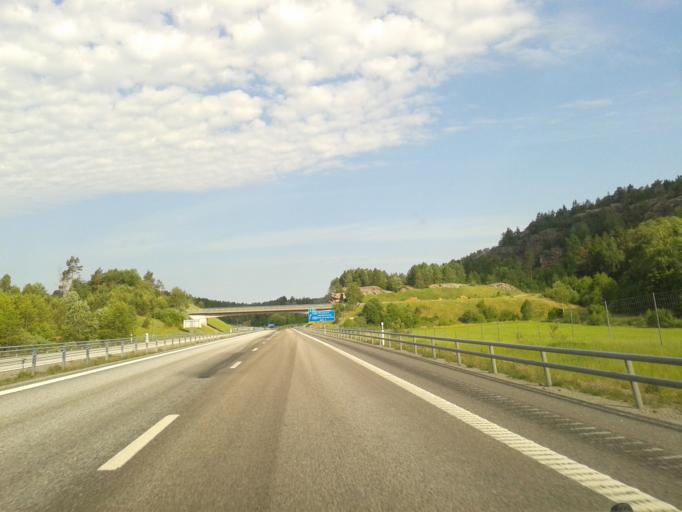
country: SE
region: Vaestra Goetaland
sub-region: Lysekils Kommun
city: Brastad
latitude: 58.5588
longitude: 11.4895
